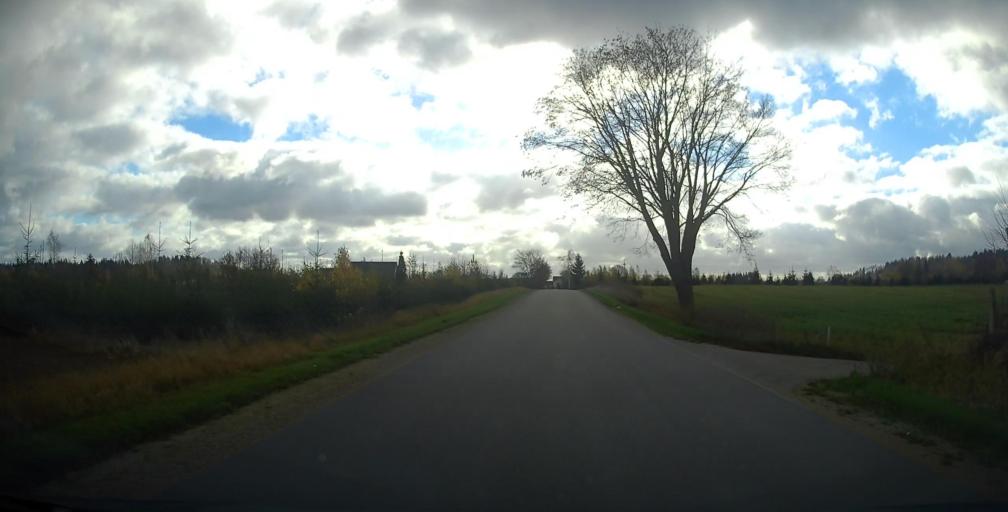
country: PL
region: Podlasie
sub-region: Suwalki
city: Suwalki
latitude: 54.2957
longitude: 22.8784
